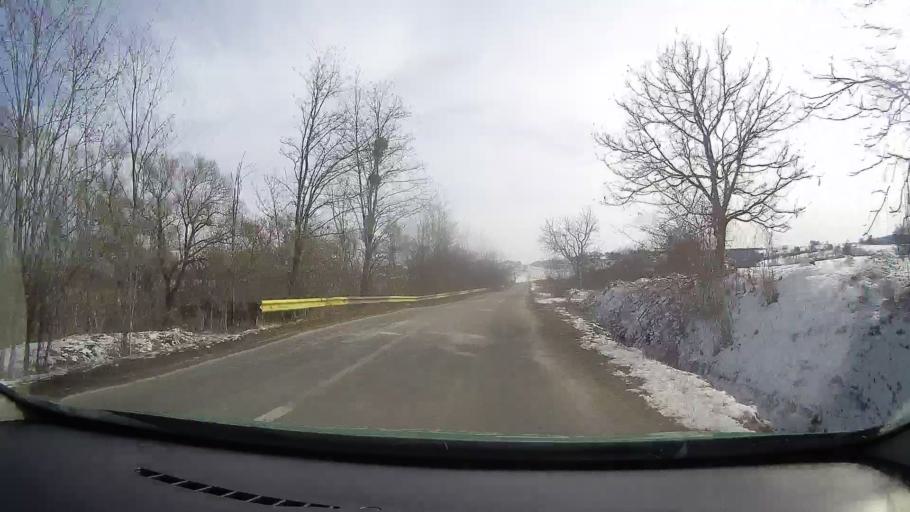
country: RO
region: Mures
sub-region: Comuna Apold
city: Apold
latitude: 46.1142
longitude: 24.8278
